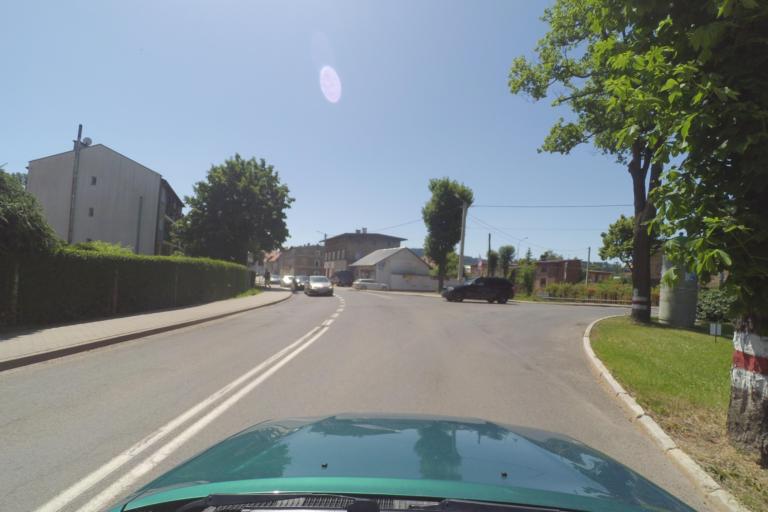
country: PL
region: Lower Silesian Voivodeship
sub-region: Powiat walbrzyski
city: Mieroszow
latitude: 50.6627
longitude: 16.1883
